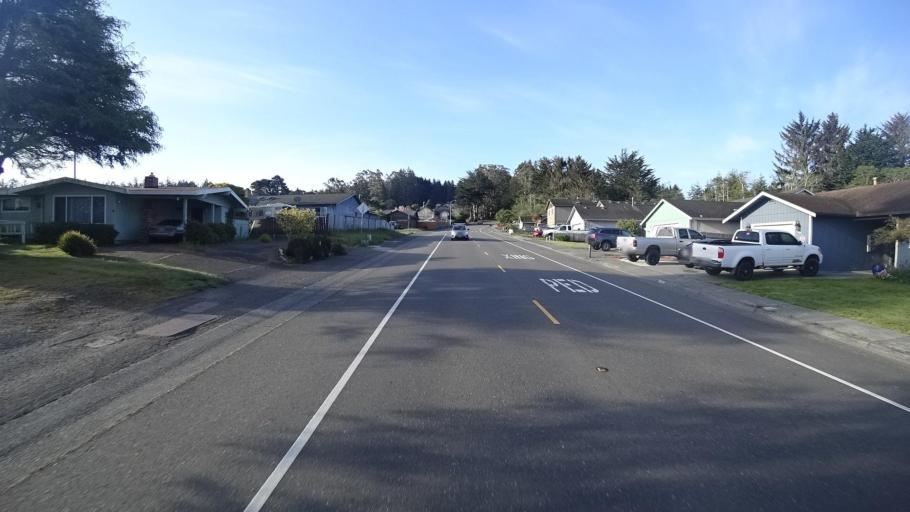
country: US
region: California
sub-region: Humboldt County
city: Humboldt Hill
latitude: 40.7312
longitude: -124.2021
